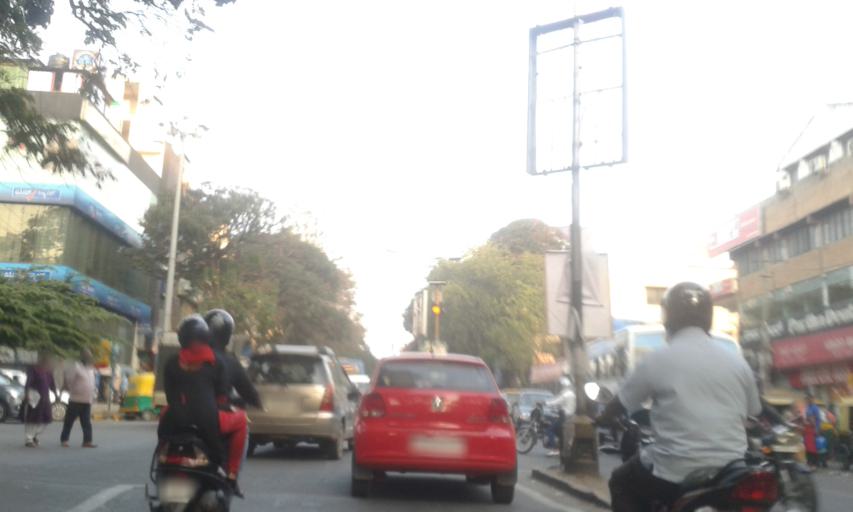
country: IN
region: Karnataka
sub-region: Bangalore Urban
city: Bangalore
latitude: 12.9169
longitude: 77.5931
